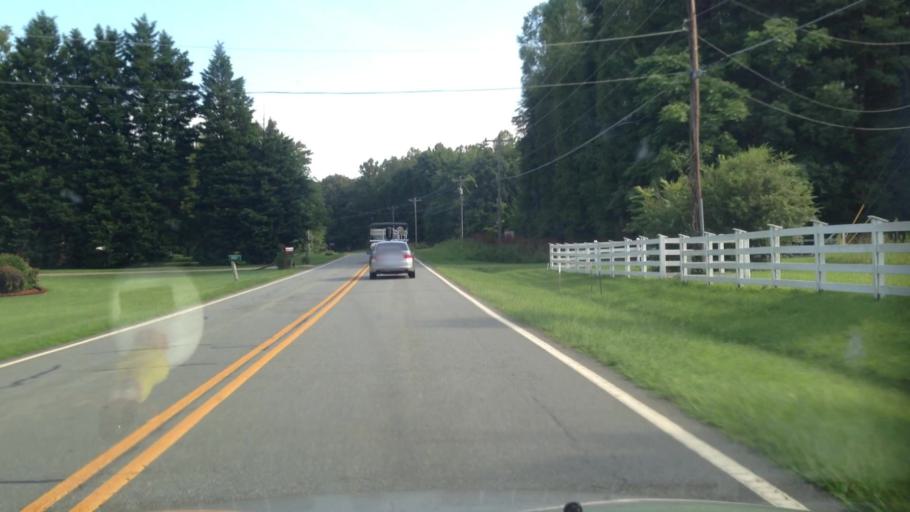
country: US
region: North Carolina
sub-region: Guilford County
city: Oak Ridge
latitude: 36.2093
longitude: -80.0551
